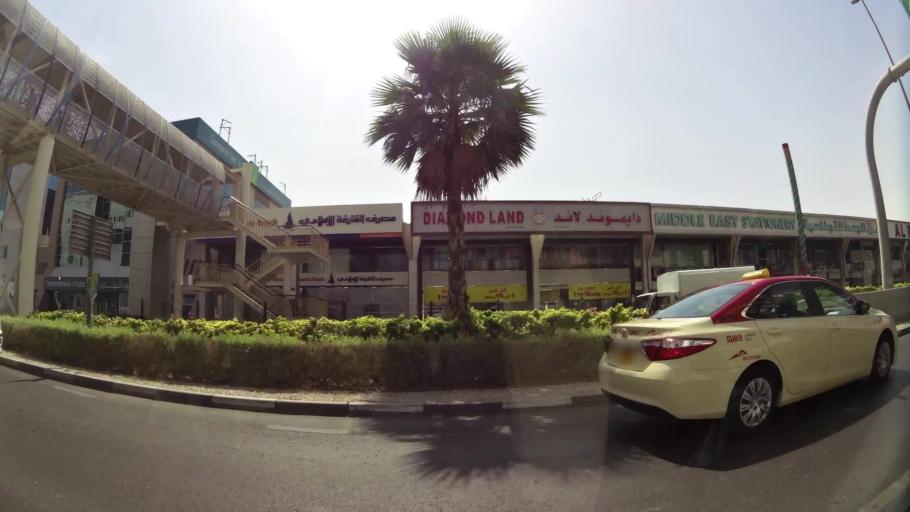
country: AE
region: Ash Shariqah
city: Sharjah
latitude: 25.2663
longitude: 55.3303
